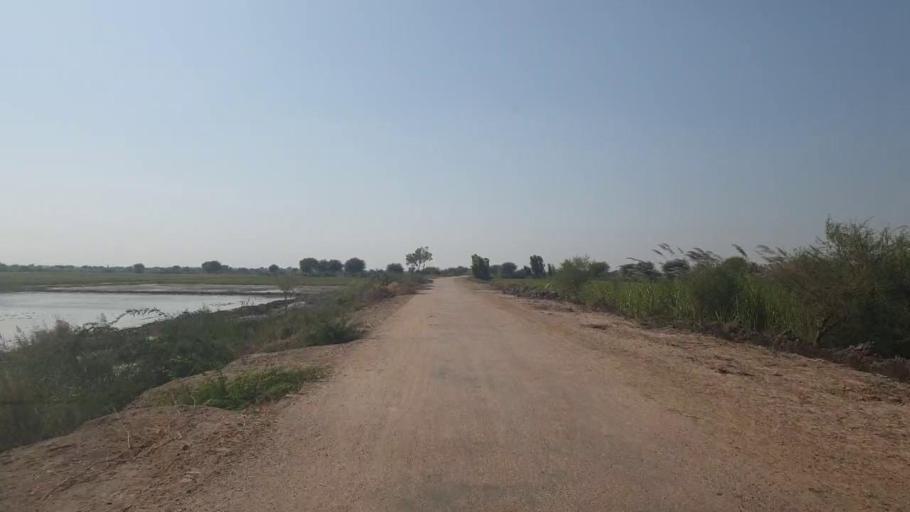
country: PK
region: Sindh
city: Badin
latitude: 24.5546
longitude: 68.8287
